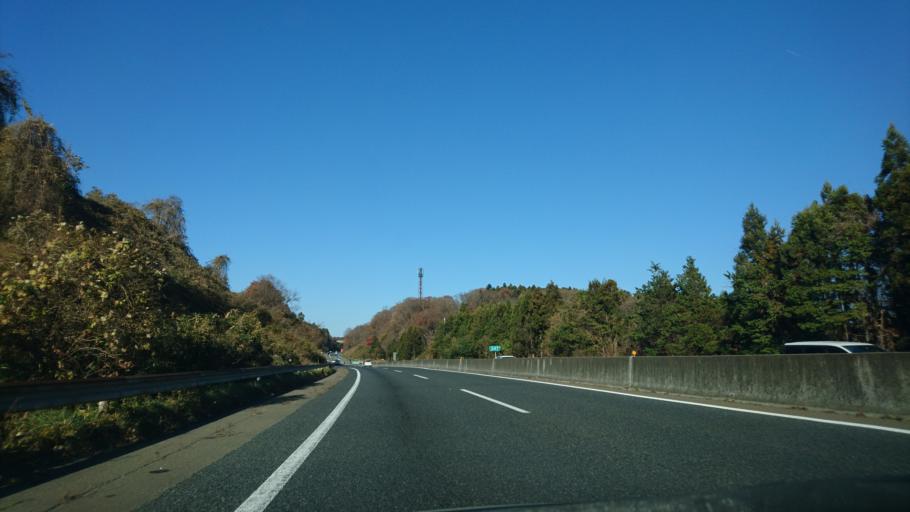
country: JP
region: Miyagi
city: Tomiya
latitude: 38.3542
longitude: 140.8815
